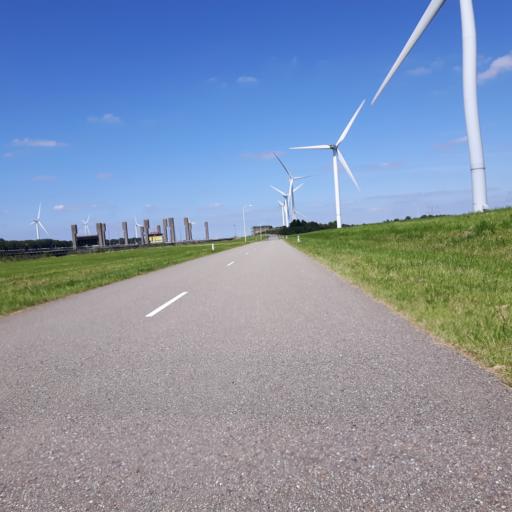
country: NL
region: North Brabant
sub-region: Gemeente Woensdrecht
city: Woensdrecht
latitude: 51.4410
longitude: 4.2346
